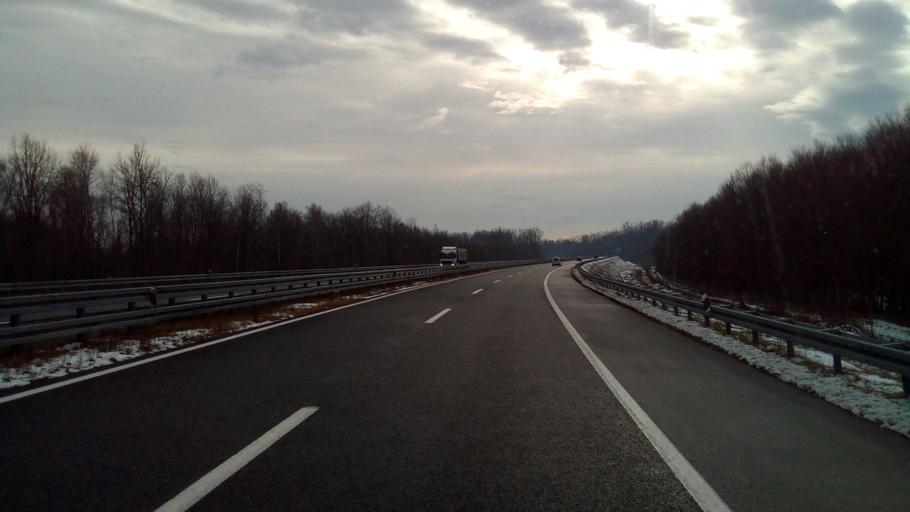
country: HR
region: Zagrebacka
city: Mraclin
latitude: 45.6354
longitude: 16.0984
